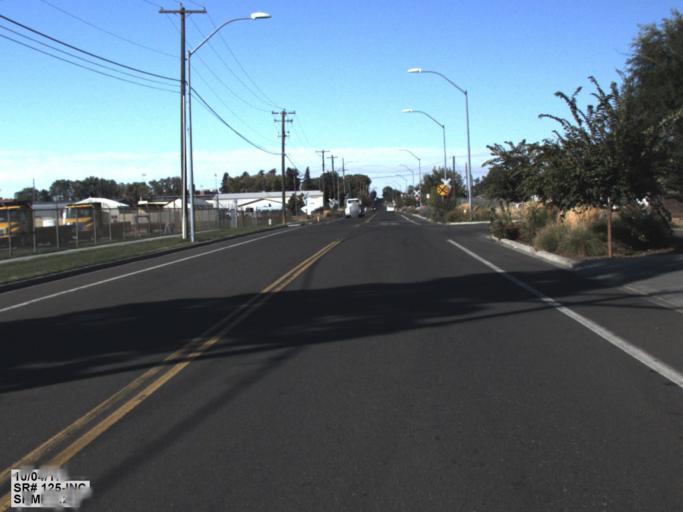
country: US
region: Washington
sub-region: Walla Walla County
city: Walla Walla
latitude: 46.0716
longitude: -118.3564
